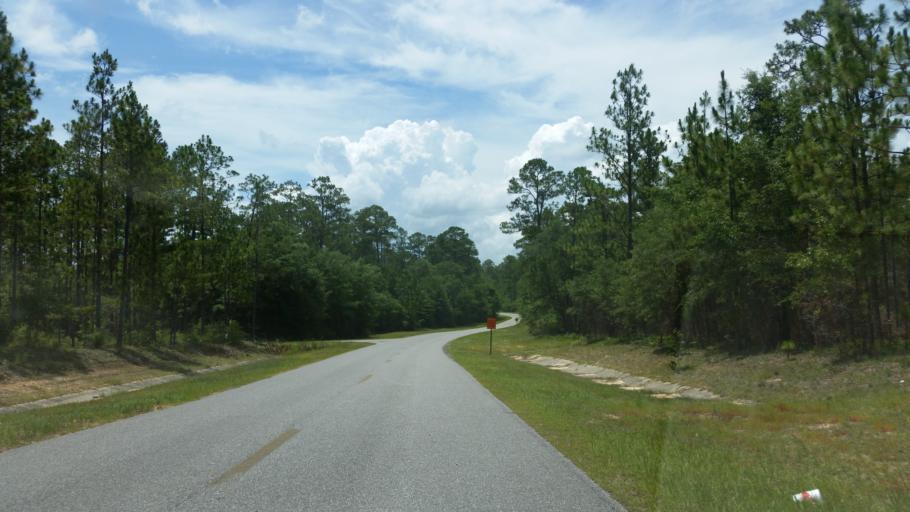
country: US
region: Florida
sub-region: Okaloosa County
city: Crestview
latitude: 30.7204
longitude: -86.7853
